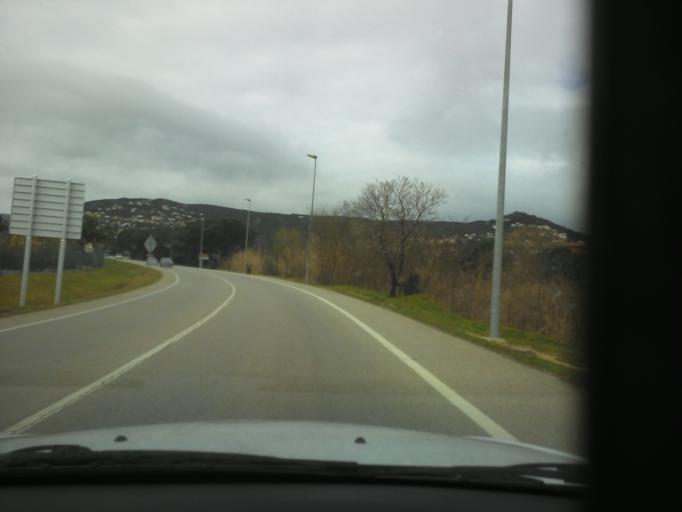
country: ES
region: Catalonia
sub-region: Provincia de Girona
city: Calonge
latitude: 41.8578
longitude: 3.0771
